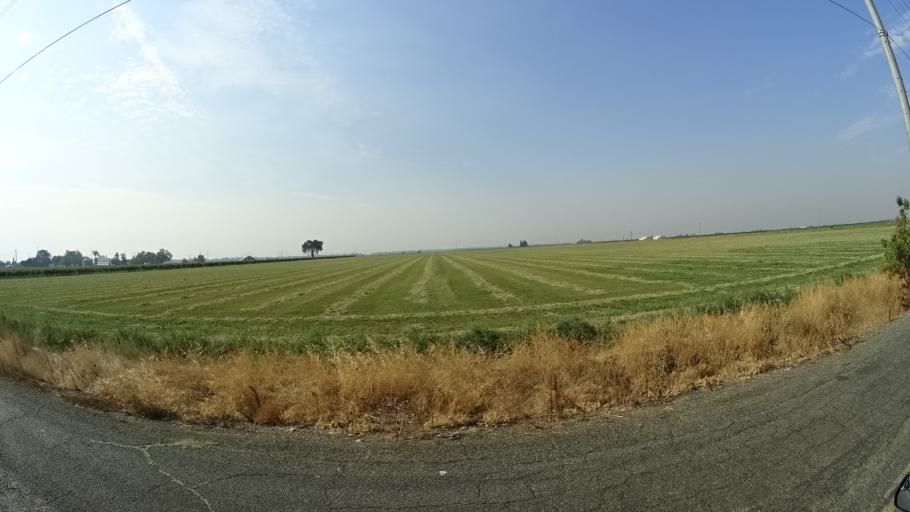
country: US
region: California
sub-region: Sacramento County
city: Elk Grove
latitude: 38.3733
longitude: -121.3616
